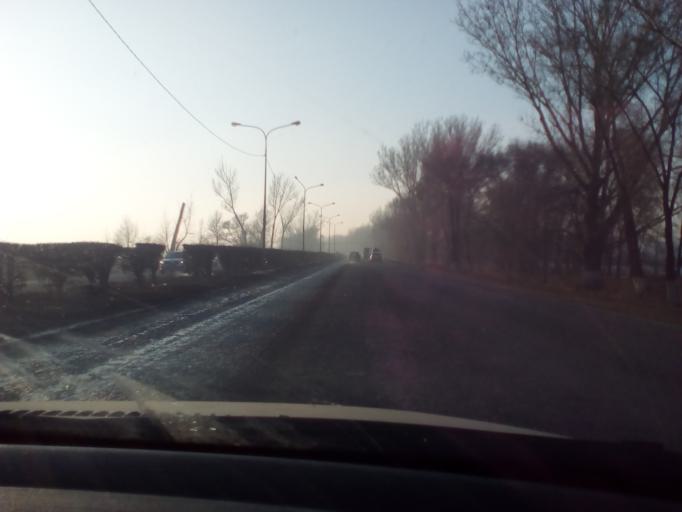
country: KZ
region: Almaty Oblysy
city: Burunday
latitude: 43.2228
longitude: 76.6141
